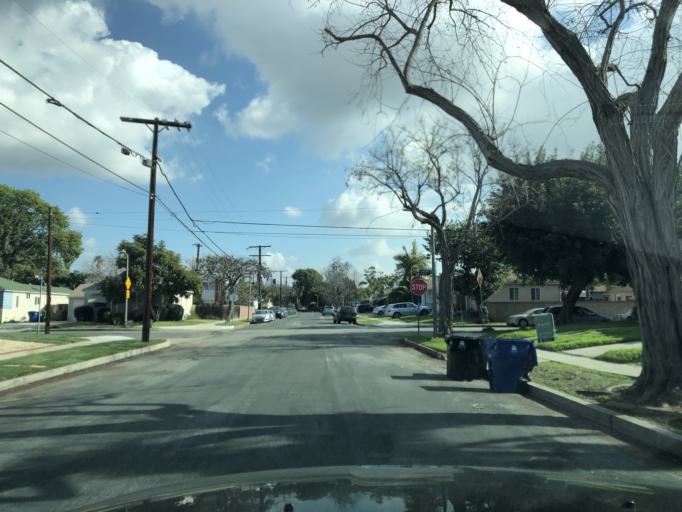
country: US
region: California
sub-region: Los Angeles County
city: Inglewood
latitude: 33.9640
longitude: -118.3740
